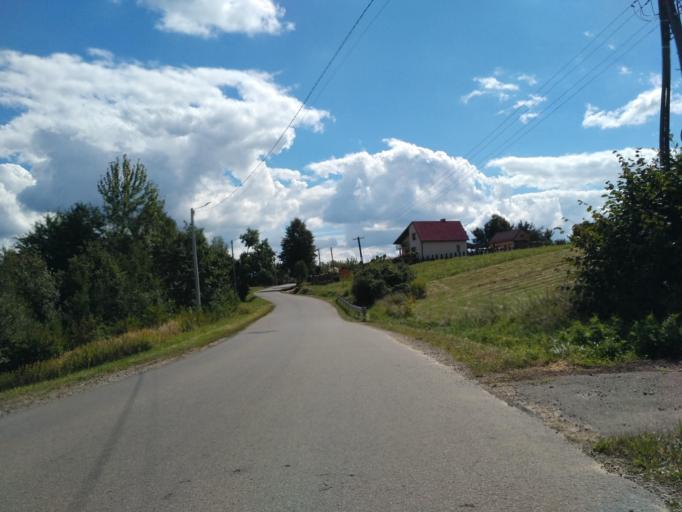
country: PL
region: Subcarpathian Voivodeship
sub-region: Powiat jasielski
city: Skolyszyn
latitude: 49.7766
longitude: 21.3660
